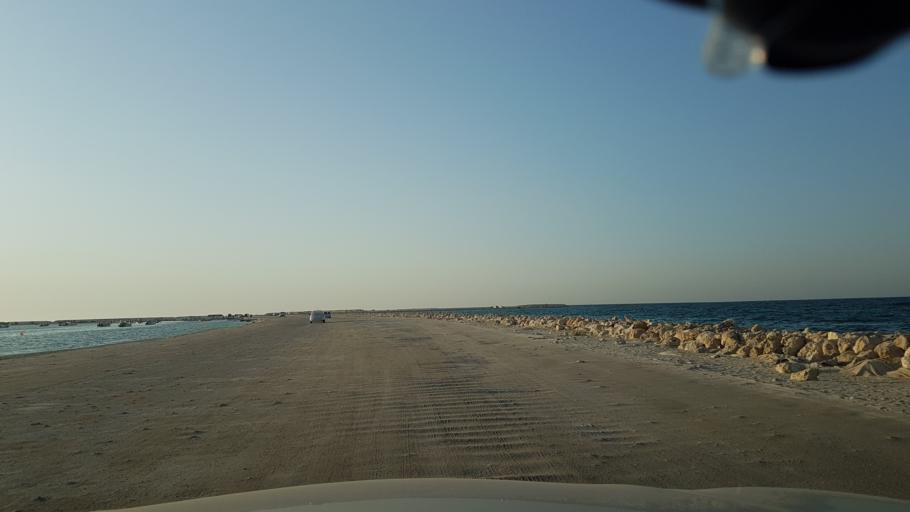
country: BH
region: Manama
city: Jidd Hafs
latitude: 26.2512
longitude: 50.5022
